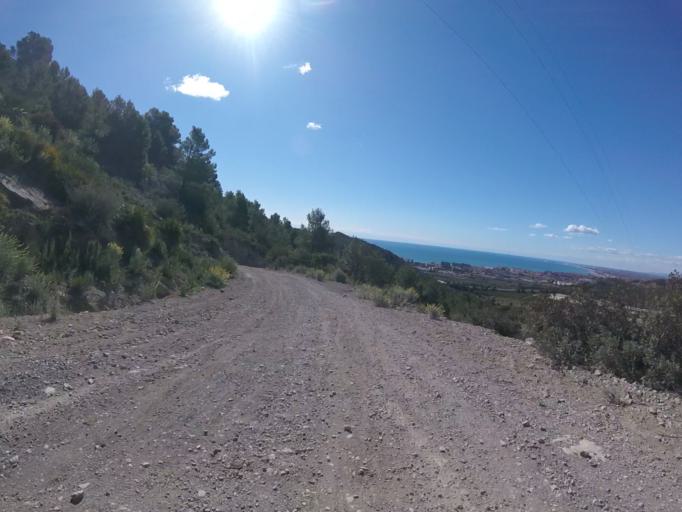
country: ES
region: Valencia
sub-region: Provincia de Castello
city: Benicassim
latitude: 40.0755
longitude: 0.0765
